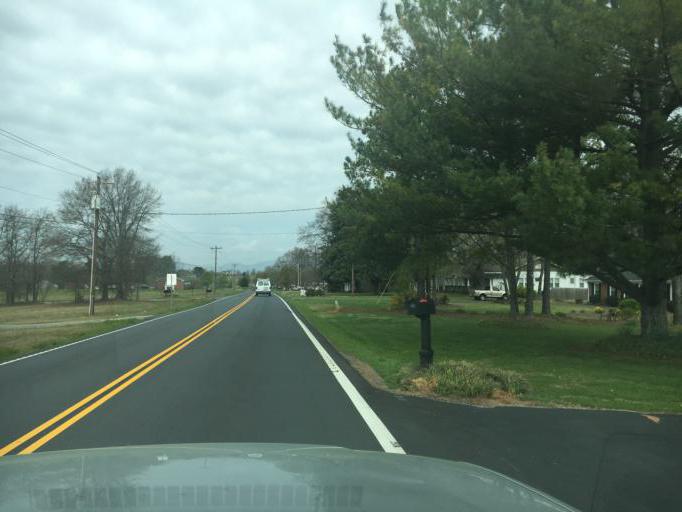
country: US
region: South Carolina
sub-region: Spartanburg County
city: Inman Mills
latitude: 35.0555
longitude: -82.1456
